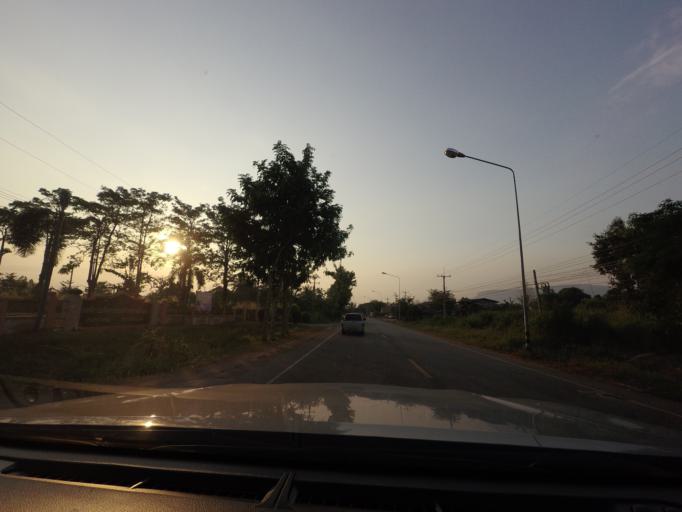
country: TH
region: Phitsanulok
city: Wang Thong
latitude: 16.7058
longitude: 100.5040
